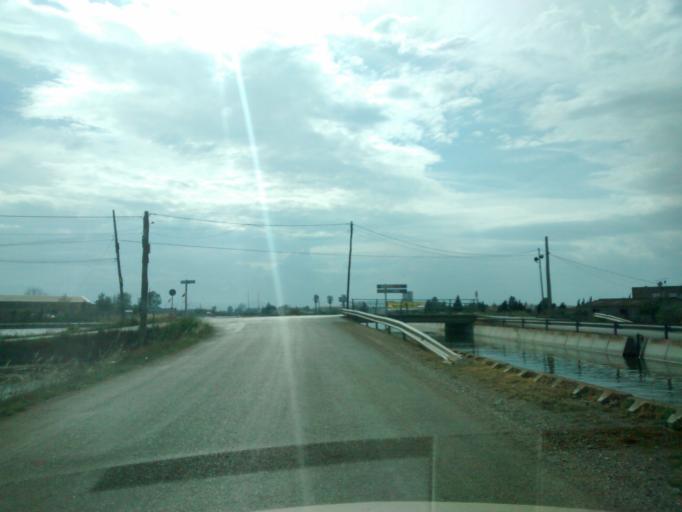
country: ES
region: Catalonia
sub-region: Provincia de Tarragona
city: Deltebre
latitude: 40.7022
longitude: 0.7308
